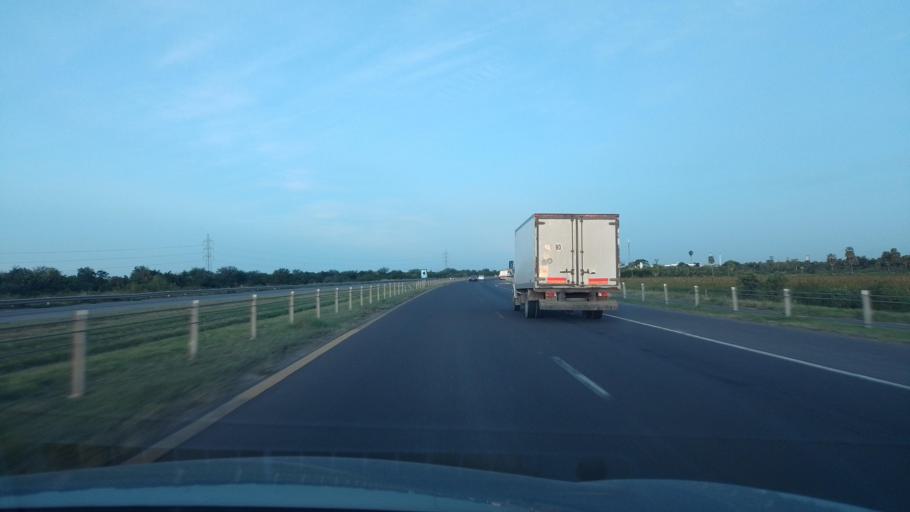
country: AR
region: Chaco
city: Barranqueras
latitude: -27.4375
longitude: -58.9003
